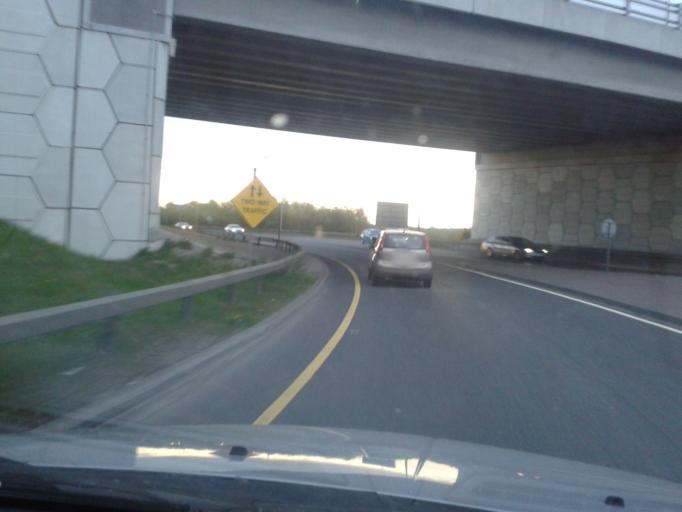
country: IE
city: Bonnybrook
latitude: 53.4105
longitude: -6.2252
